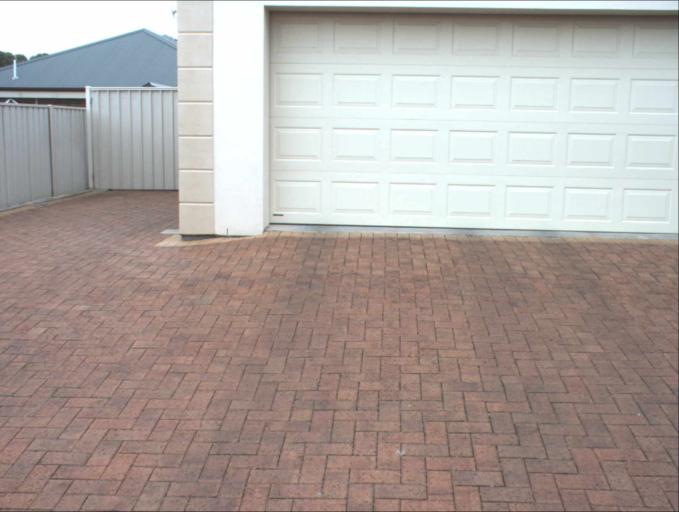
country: AU
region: South Australia
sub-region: Port Adelaide Enfield
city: Gilles Plains
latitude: -34.8563
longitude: 138.6332
